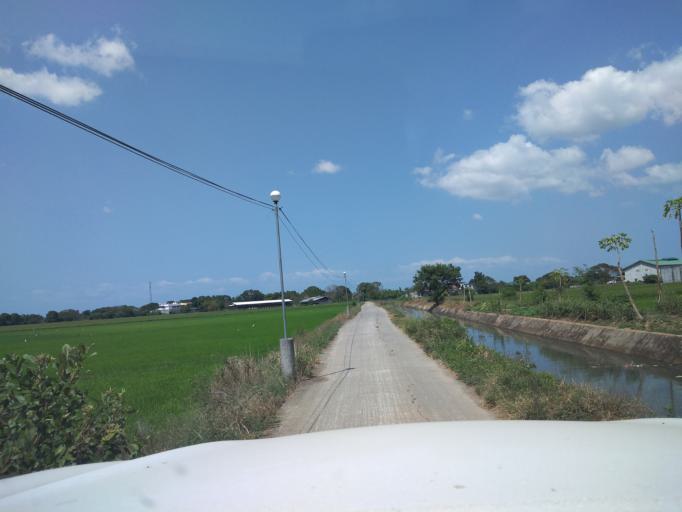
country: PH
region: Central Luzon
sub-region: Province of Pampanga
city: Bahay Pare
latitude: 15.0459
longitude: 120.8746
